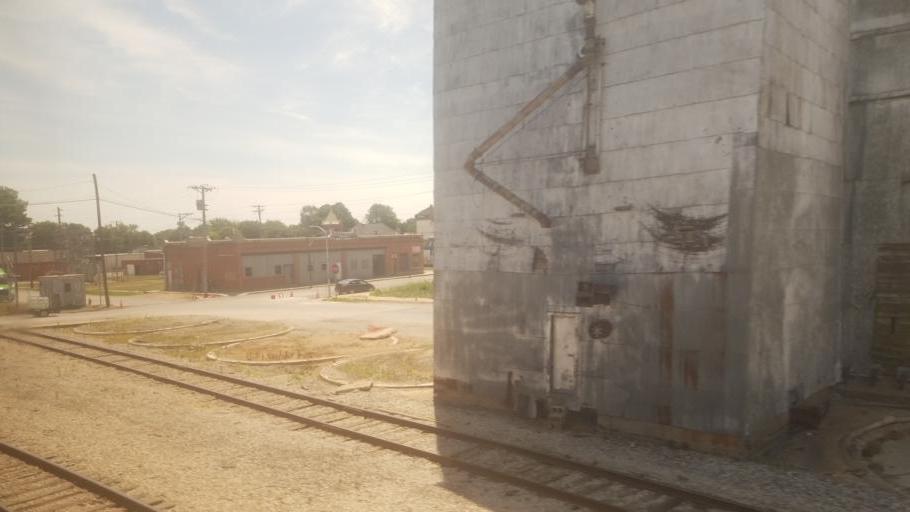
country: US
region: Missouri
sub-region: Carroll County
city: Carrollton
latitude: 39.3034
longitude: -93.6777
